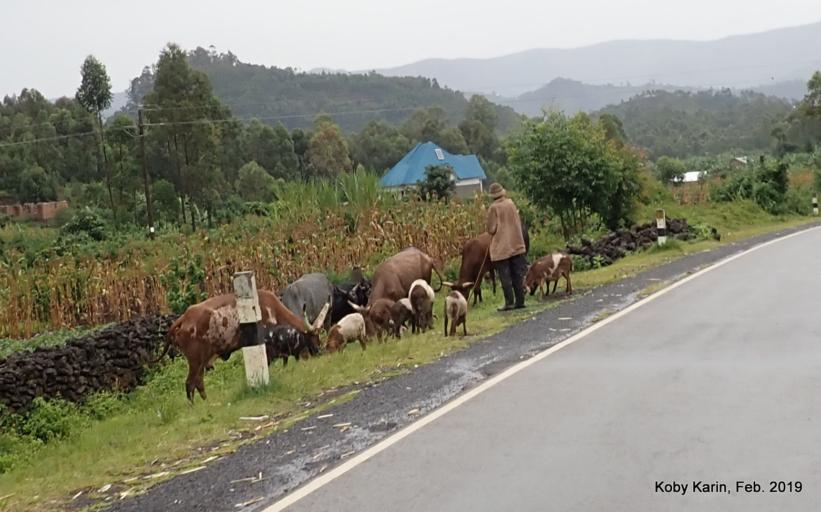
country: UG
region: Western Region
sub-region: Kisoro District
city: Kisoro
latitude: -1.3296
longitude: 29.7300
